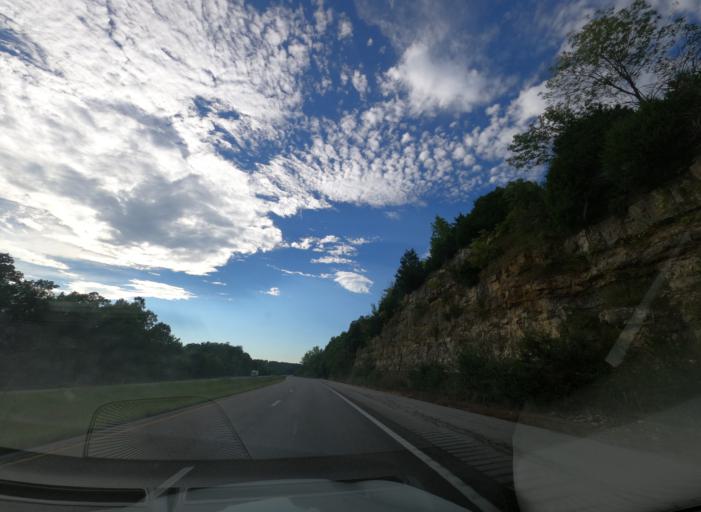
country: US
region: Missouri
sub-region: Jefferson County
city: Crystal City
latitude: 38.1458
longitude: -90.3397
